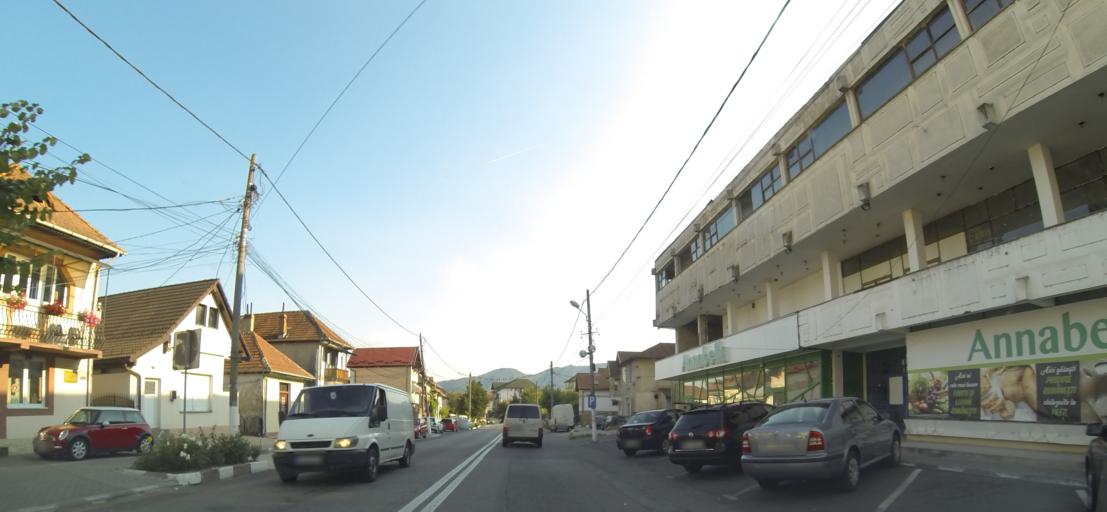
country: RO
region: Valcea
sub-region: Oras Calimanesti
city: Jiblea Veche
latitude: 45.2448
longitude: 24.3394
